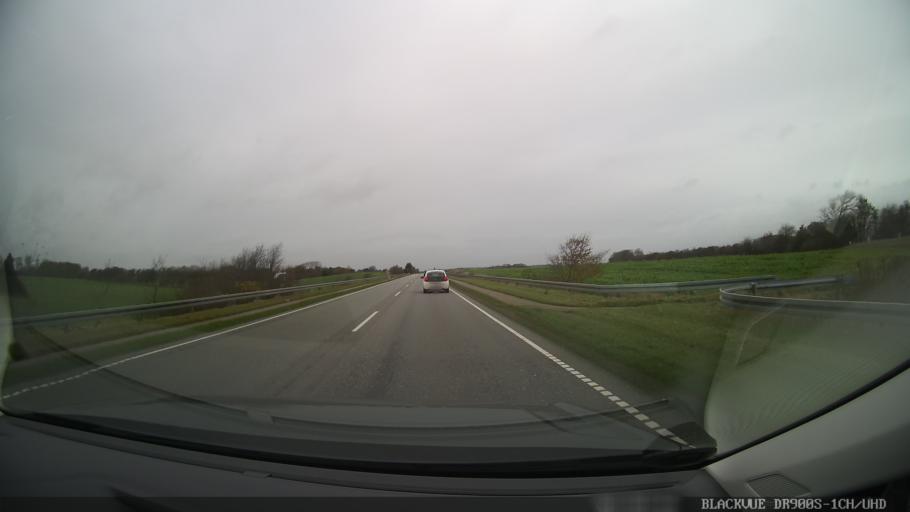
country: DK
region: North Denmark
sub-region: Thisted Kommune
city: Thisted
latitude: 56.8403
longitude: 8.7030
